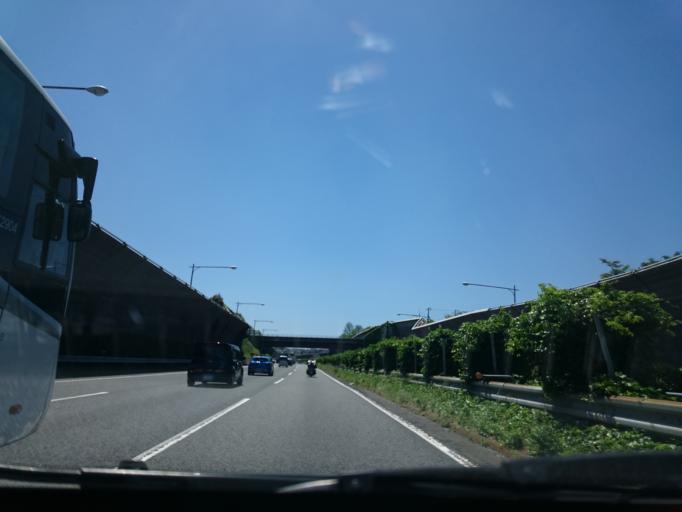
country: JP
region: Kanagawa
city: Isehara
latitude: 35.3780
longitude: 139.2677
